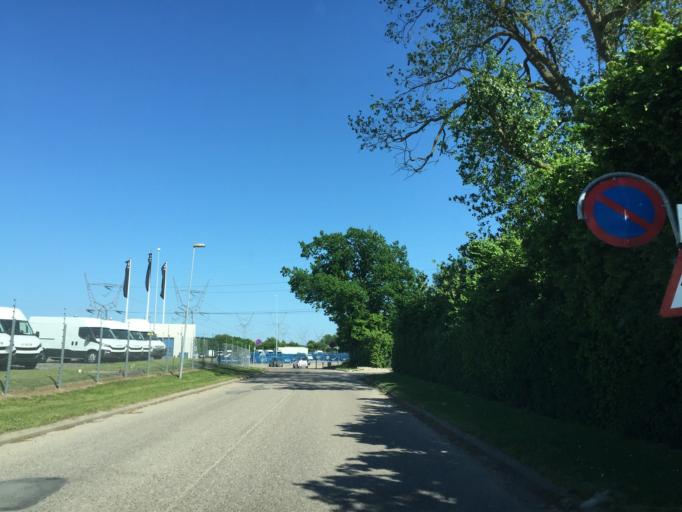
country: DK
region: South Denmark
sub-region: Odense Kommune
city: Hojby
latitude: 55.3494
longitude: 10.4142
